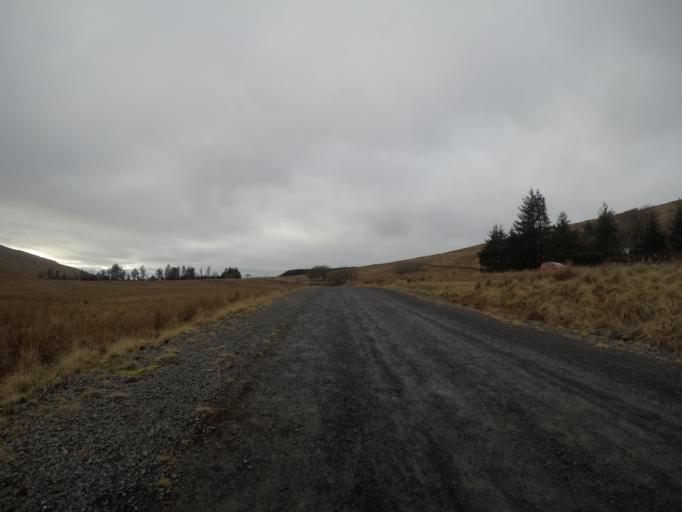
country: GB
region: Scotland
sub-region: North Ayrshire
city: Fairlie
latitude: 55.7789
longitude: -4.8059
